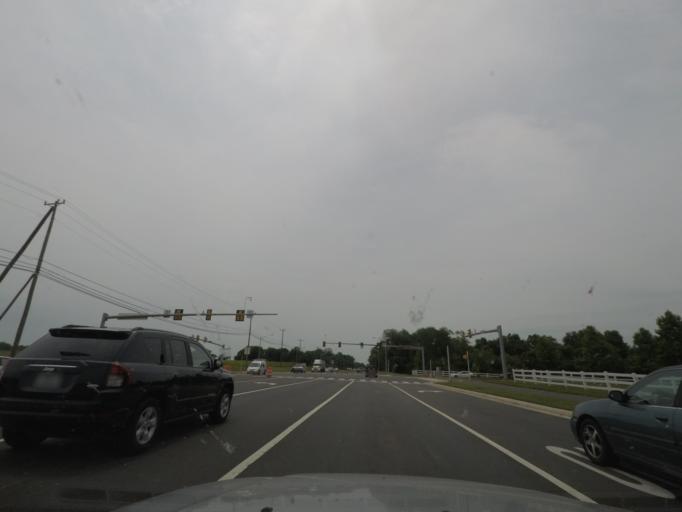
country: US
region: Virginia
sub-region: Loudoun County
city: Leesburg
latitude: 39.0917
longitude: -77.5840
